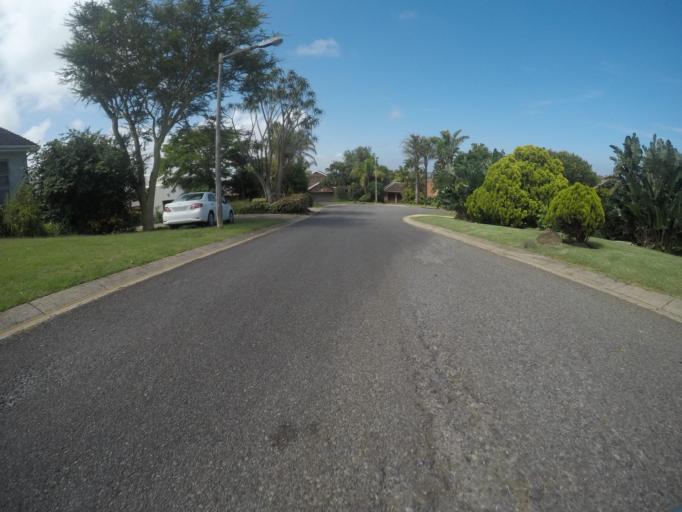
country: ZA
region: Eastern Cape
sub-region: Buffalo City Metropolitan Municipality
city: East London
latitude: -32.9717
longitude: 27.9073
